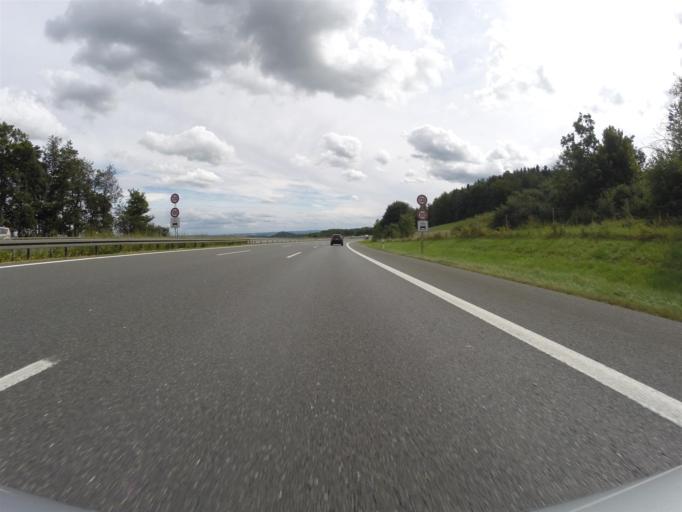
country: DE
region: Bavaria
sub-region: Upper Franconia
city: Pegnitz
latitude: 49.7845
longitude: 11.5120
